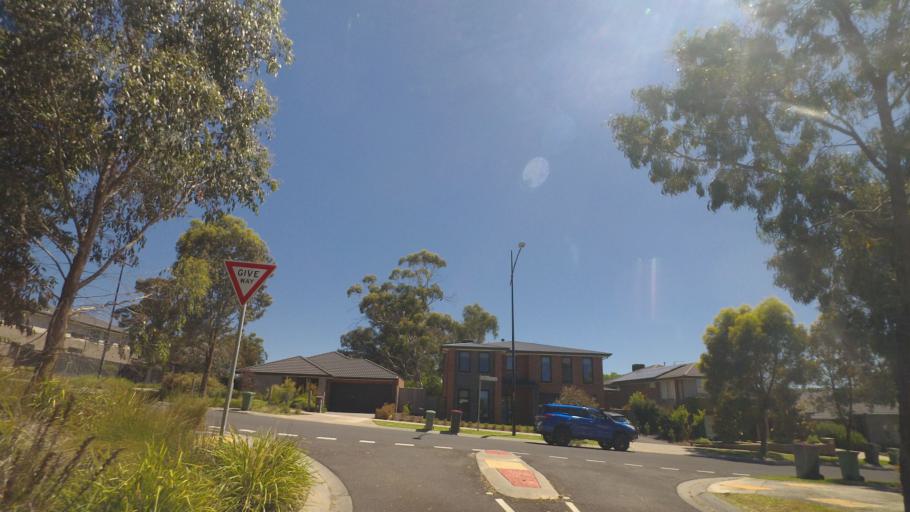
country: AU
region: Victoria
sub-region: Maroondah
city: Croydon North
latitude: -37.7790
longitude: 145.2996
